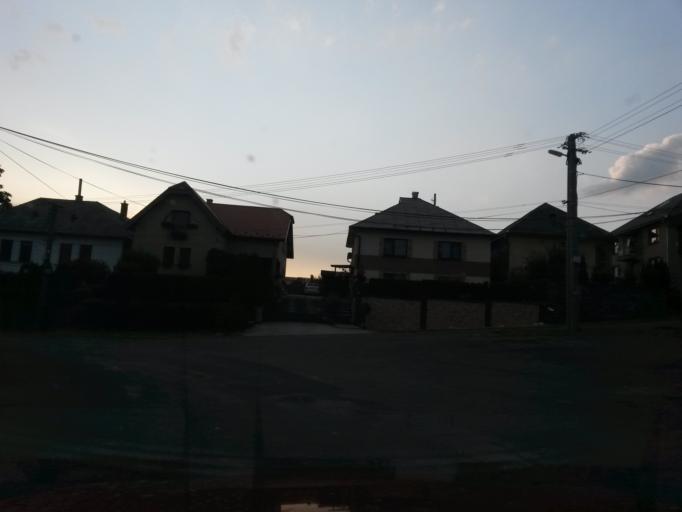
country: SK
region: Kosicky
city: Kosice
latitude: 48.7686
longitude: 21.4468
